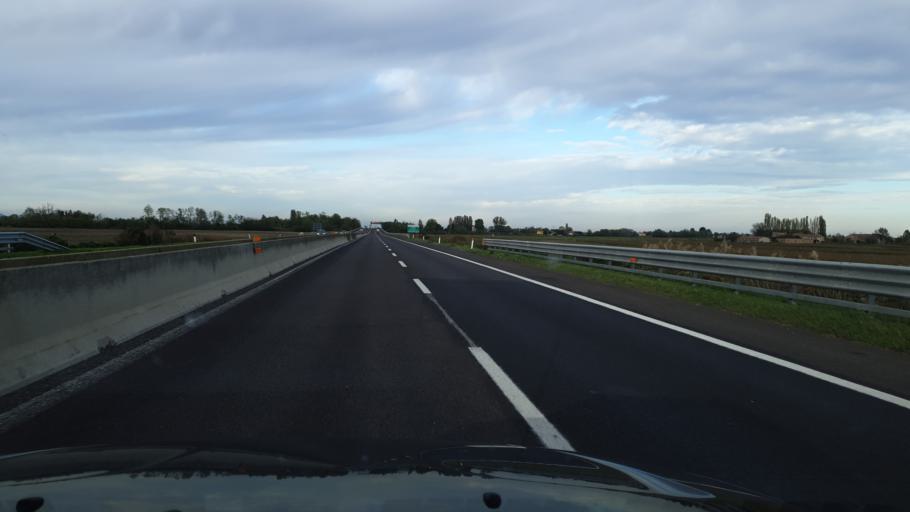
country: IT
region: Veneto
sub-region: Provincia di Rovigo
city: Grignano Polesine
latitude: 45.0638
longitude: 11.7276
